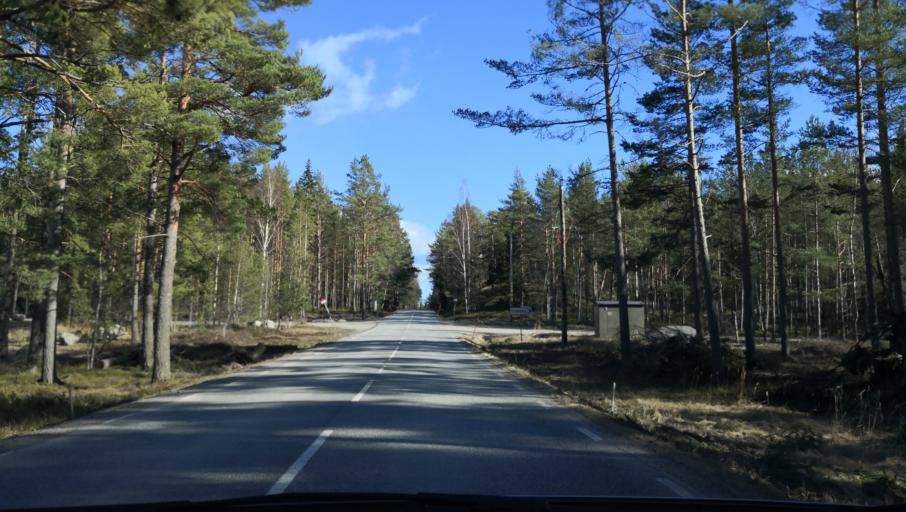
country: SE
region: Stockholm
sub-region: Varmdo Kommun
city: Hemmesta
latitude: 59.3571
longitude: 18.5906
